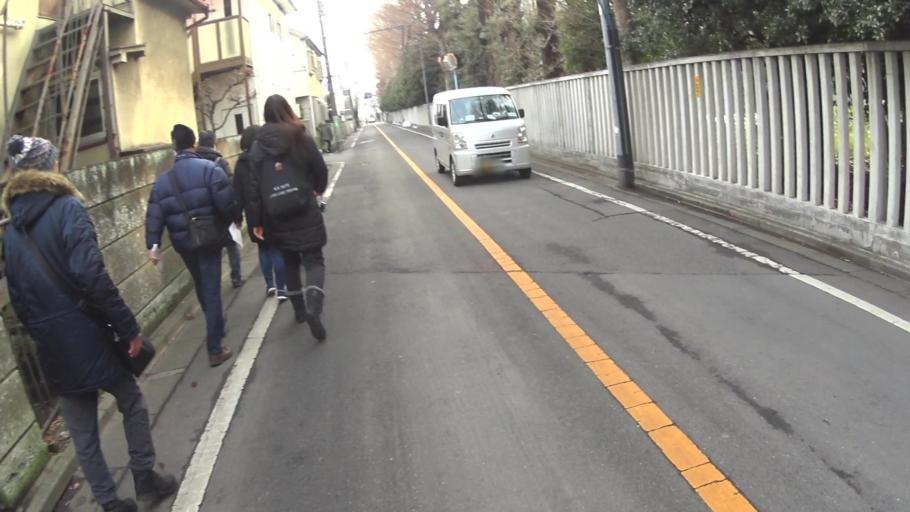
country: JP
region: Tokyo
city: Musashino
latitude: 35.7106
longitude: 139.5922
